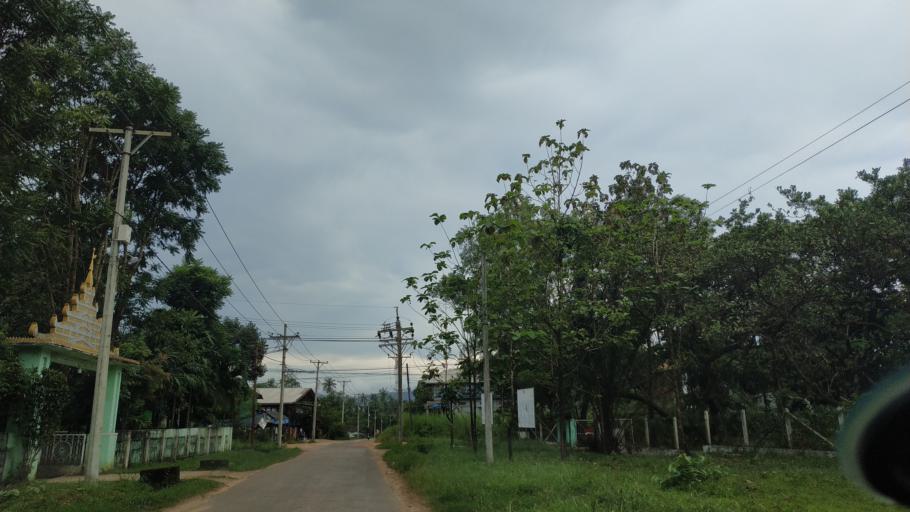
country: MM
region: Tanintharyi
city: Dawei
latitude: 14.0984
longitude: 98.1997
